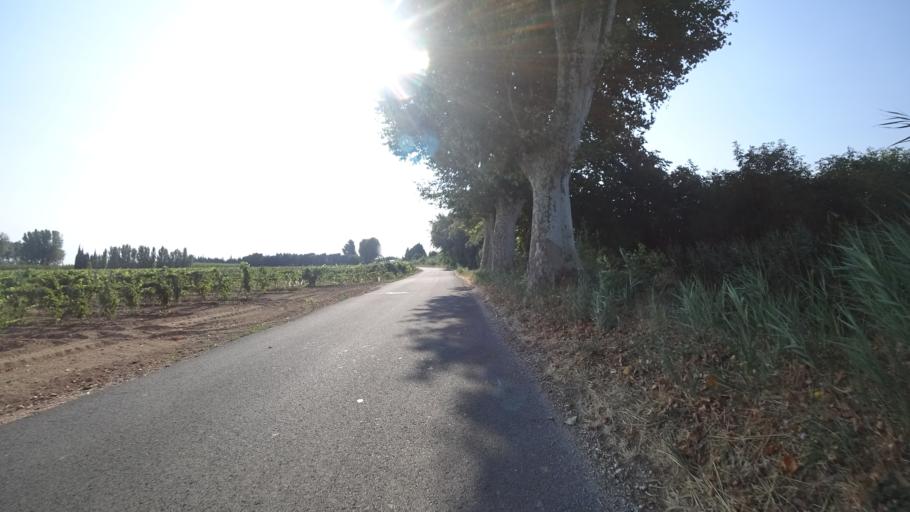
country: FR
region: Languedoc-Roussillon
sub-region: Departement des Pyrenees-Orientales
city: Claira
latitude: 42.7590
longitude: 2.9669
